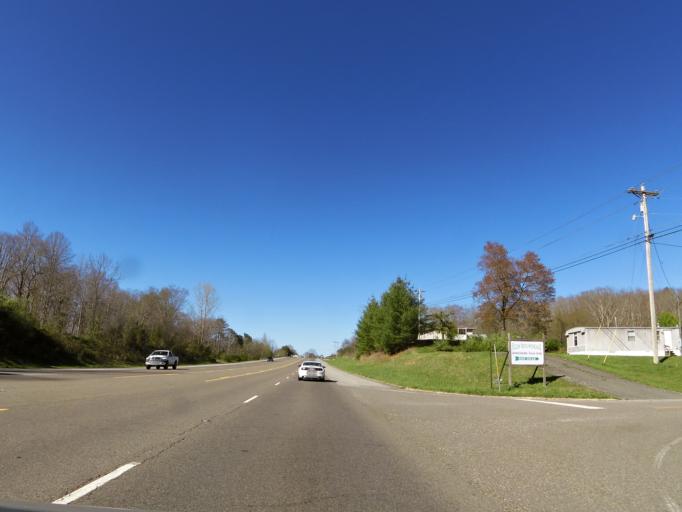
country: US
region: Tennessee
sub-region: Scott County
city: Oneida
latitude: 36.4659
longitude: -84.5469
